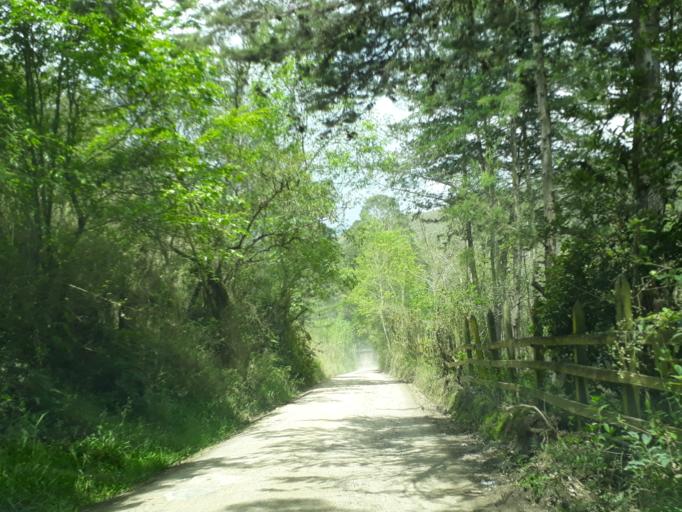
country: CO
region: Cundinamarca
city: Macheta
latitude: 5.0846
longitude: -73.5751
